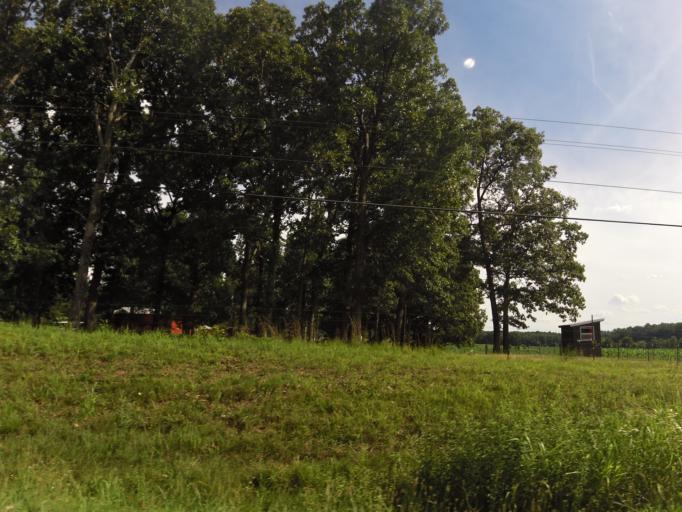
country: US
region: Tennessee
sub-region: Carroll County
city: Huntingdon
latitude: 36.0312
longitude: -88.3426
